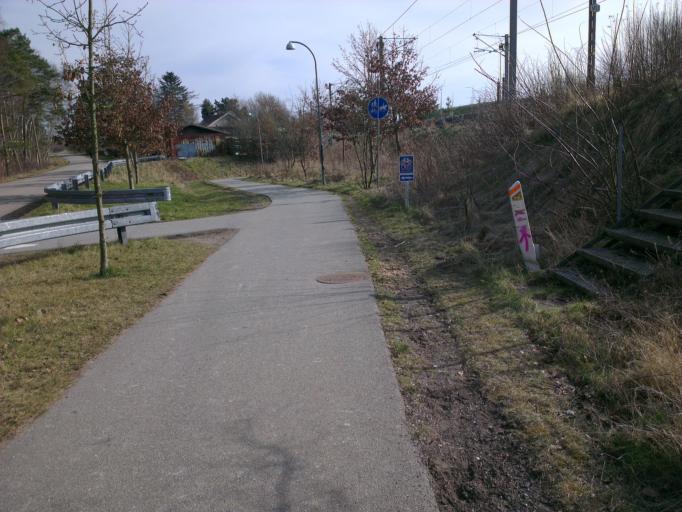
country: DK
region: Capital Region
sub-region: Egedal Kommune
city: Olstykke
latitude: 55.7927
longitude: 12.1670
